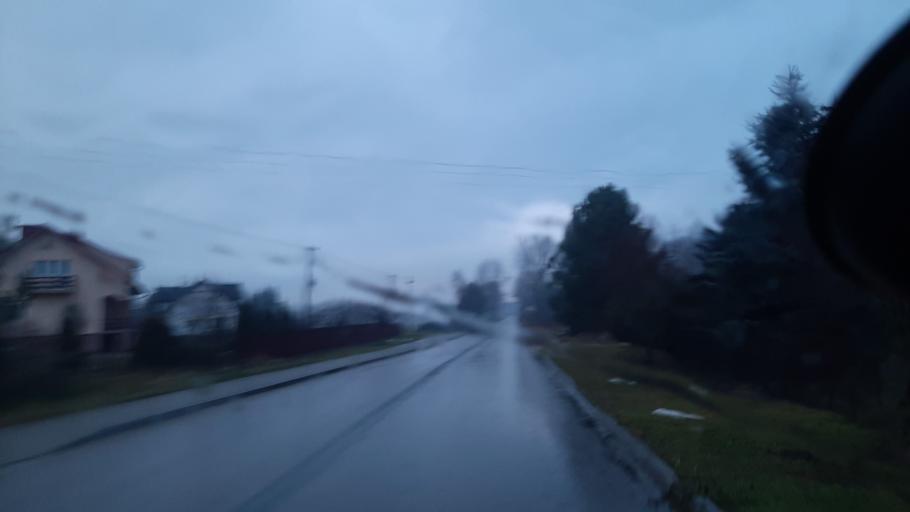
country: PL
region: Lublin Voivodeship
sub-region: Powiat lubartowski
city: Firlej
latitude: 51.5489
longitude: 22.5545
